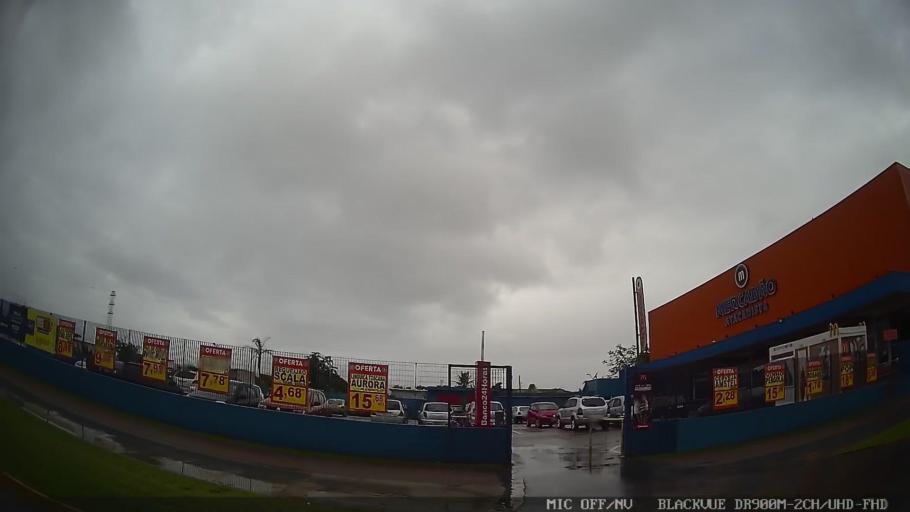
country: BR
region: Sao Paulo
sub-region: Itanhaem
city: Itanhaem
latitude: -24.1758
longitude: -46.7786
